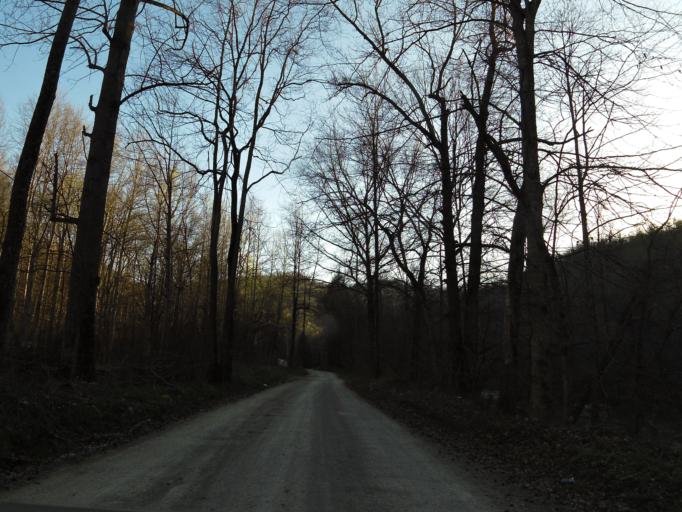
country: US
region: Tennessee
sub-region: Campbell County
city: Caryville
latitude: 36.2638
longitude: -84.3502
